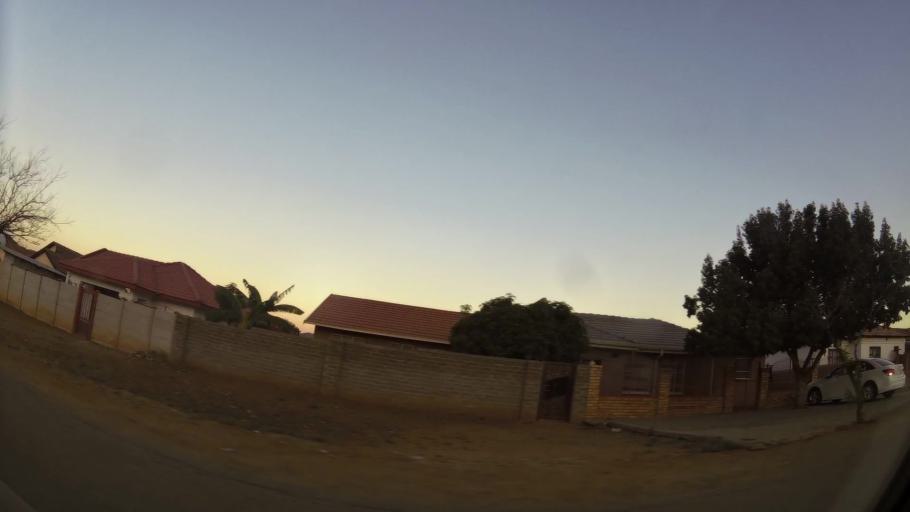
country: ZA
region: North-West
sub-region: Bojanala Platinum District Municipality
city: Rustenburg
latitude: -25.6482
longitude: 27.2073
